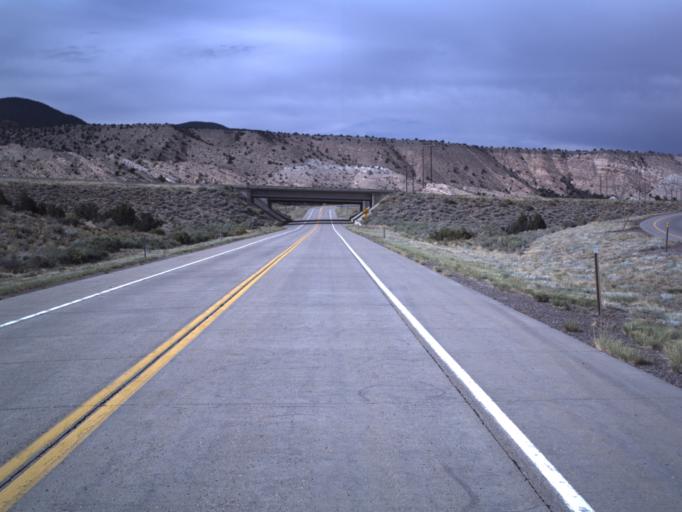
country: US
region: Utah
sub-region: Sevier County
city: Monroe
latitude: 38.5974
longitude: -112.2543
